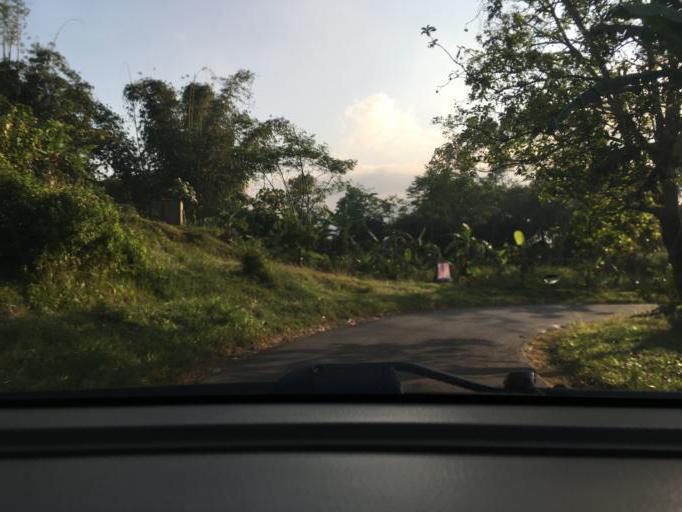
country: ID
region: West Java
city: Maniis
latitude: -7.0359
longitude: 108.3223
